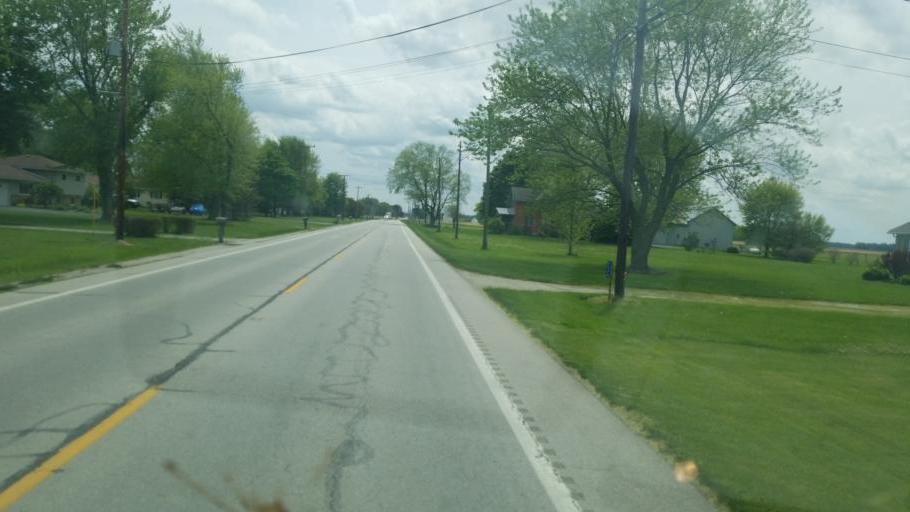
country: US
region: Ohio
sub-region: Seneca County
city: Tiffin
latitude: 41.1995
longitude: -83.1677
